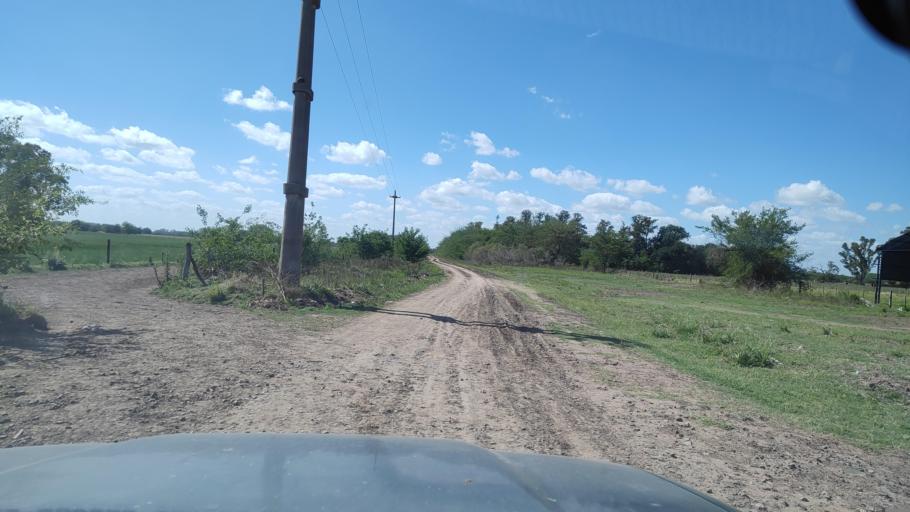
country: AR
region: Buenos Aires
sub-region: Partido de Lujan
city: Lujan
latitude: -34.5279
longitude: -59.1530
